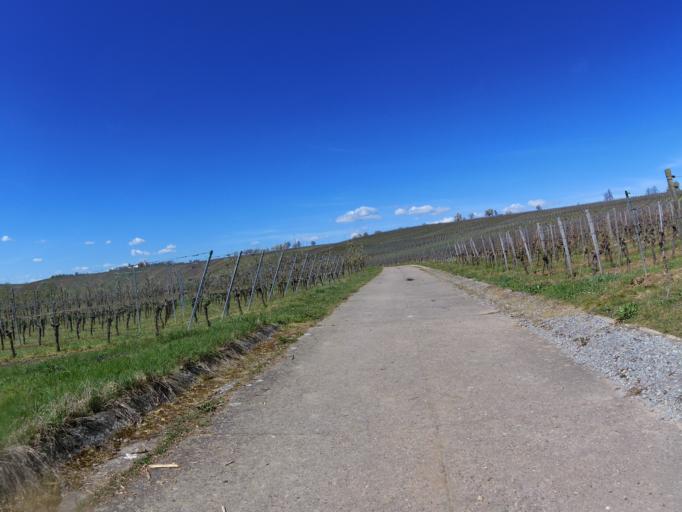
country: DE
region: Bavaria
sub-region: Regierungsbezirk Unterfranken
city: Nordheim
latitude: 49.8611
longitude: 10.2040
